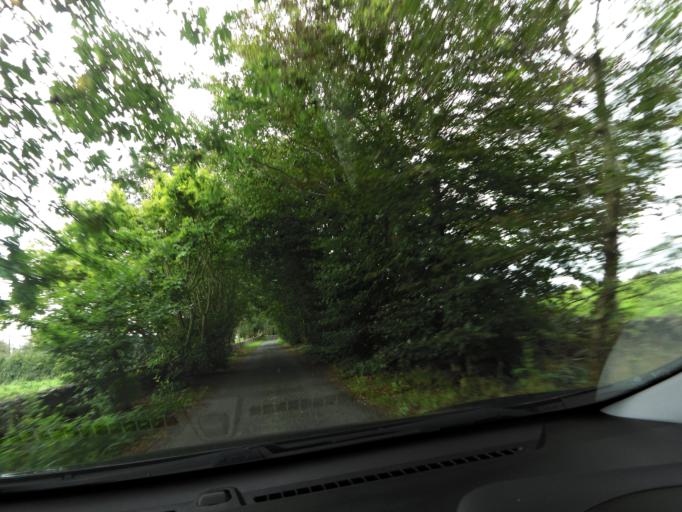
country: IE
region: Connaught
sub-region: County Galway
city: Loughrea
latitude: 53.2782
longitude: -8.6357
